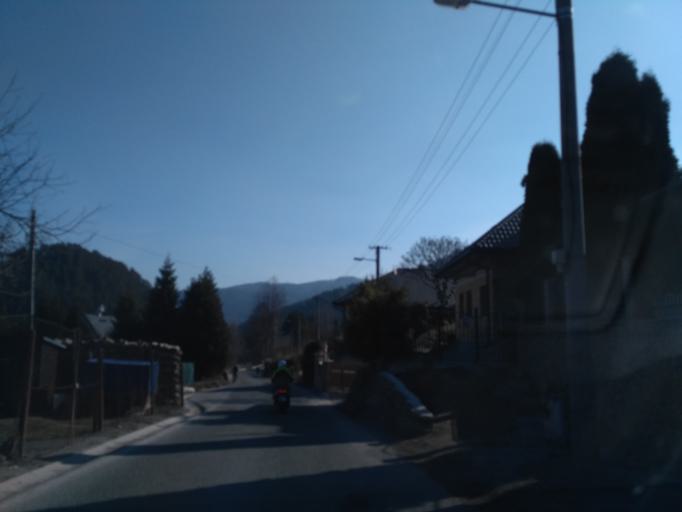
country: SK
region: Kosicky
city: Medzev
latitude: 48.7316
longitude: 20.7434
